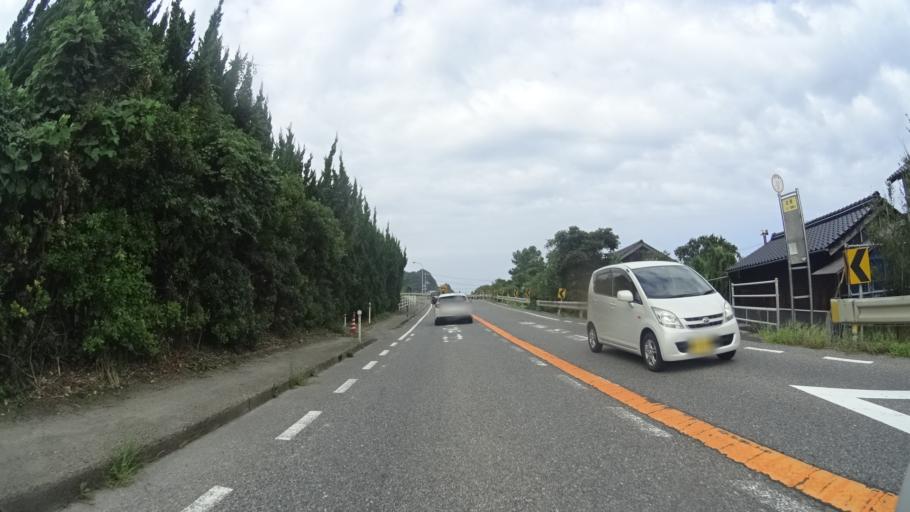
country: JP
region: Shimane
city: Odacho-oda
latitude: 35.1581
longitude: 132.4073
